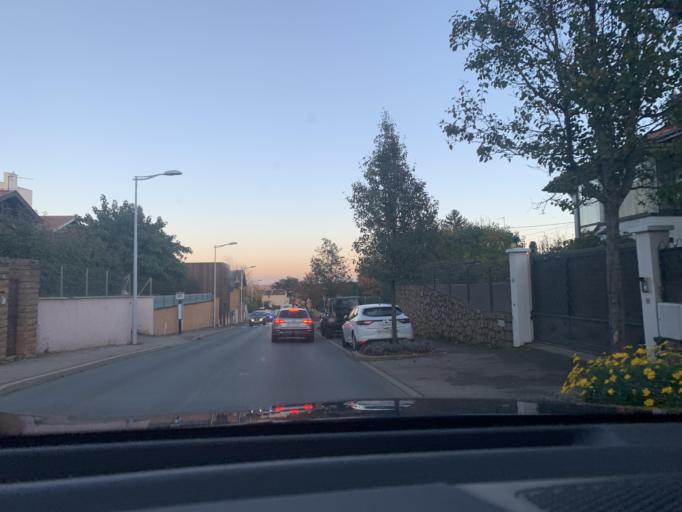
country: FR
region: Rhone-Alpes
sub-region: Departement du Rhone
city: Limas
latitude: 45.9783
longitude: 4.7098
